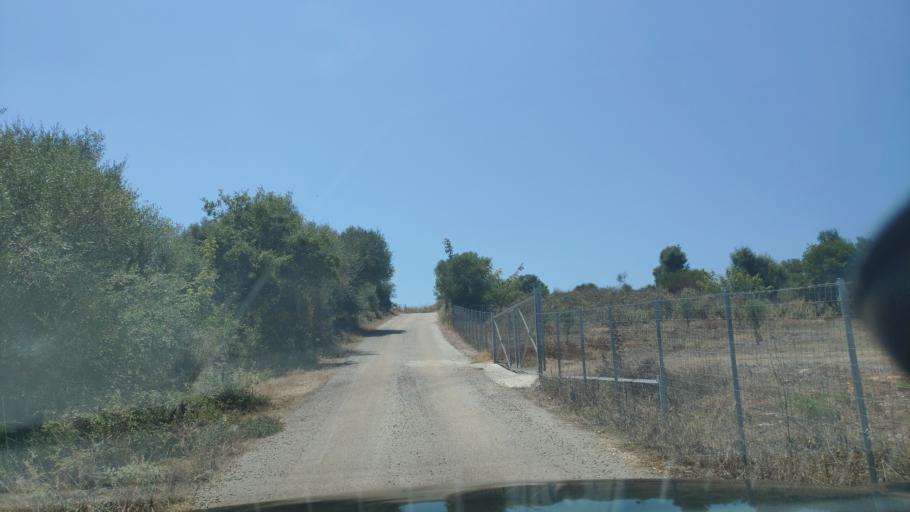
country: GR
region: West Greece
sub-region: Nomos Aitolias kai Akarnanias
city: Amfilochia
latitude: 38.9071
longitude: 21.1010
